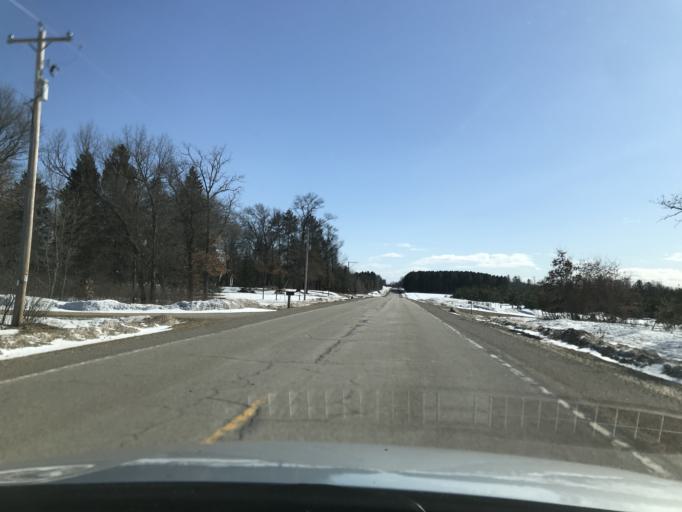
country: US
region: Wisconsin
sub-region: Marinette County
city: Niagara
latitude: 45.3521
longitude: -88.1012
